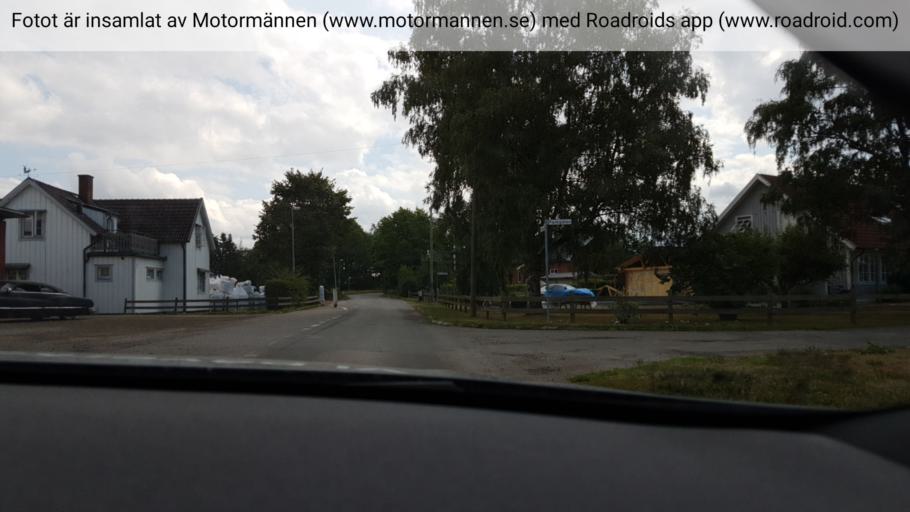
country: SE
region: Vaestra Goetaland
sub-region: Falkopings Kommun
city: Falkoeping
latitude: 58.0884
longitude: 13.5184
